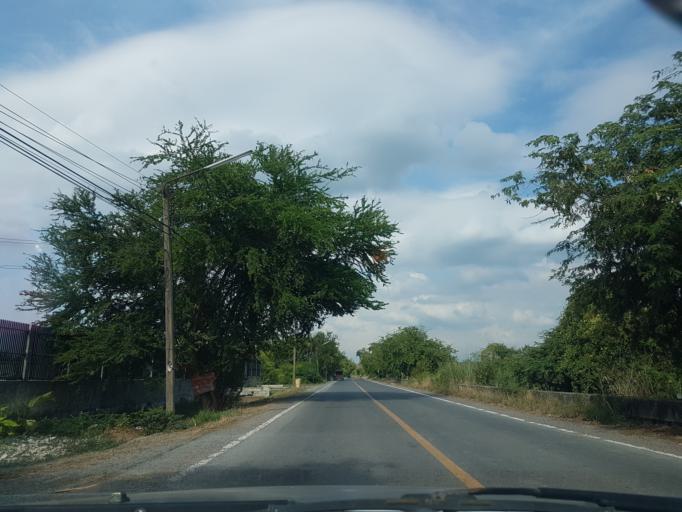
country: TH
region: Pathum Thani
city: Nong Suea
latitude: 14.1469
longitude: 100.8914
